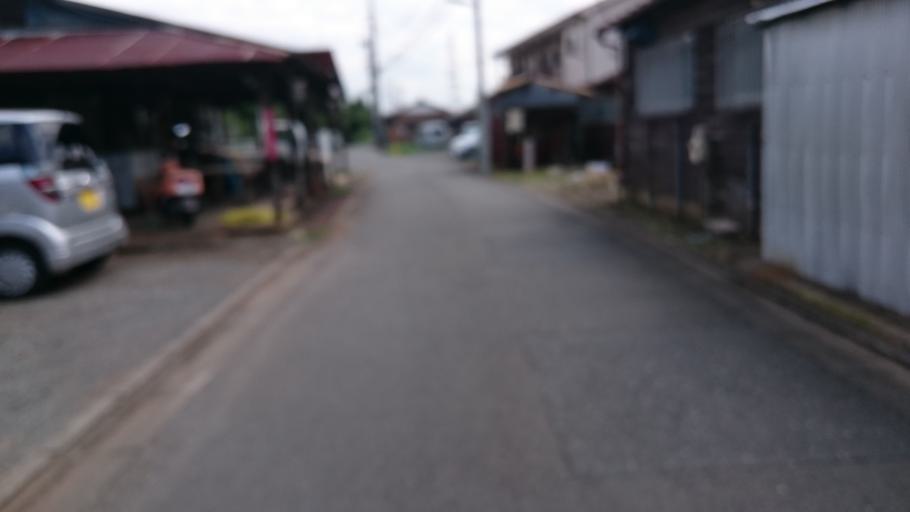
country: JP
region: Tokyo
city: Kokubunji
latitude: 35.6836
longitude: 139.4886
